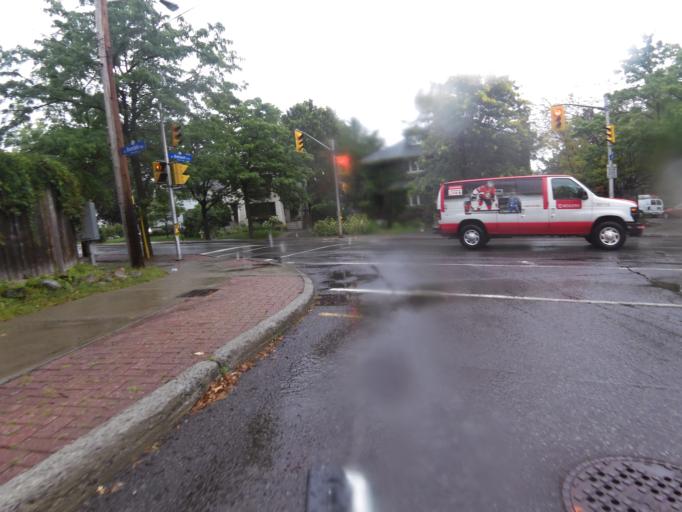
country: CA
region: Ontario
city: Ottawa
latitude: 45.3943
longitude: -75.6791
